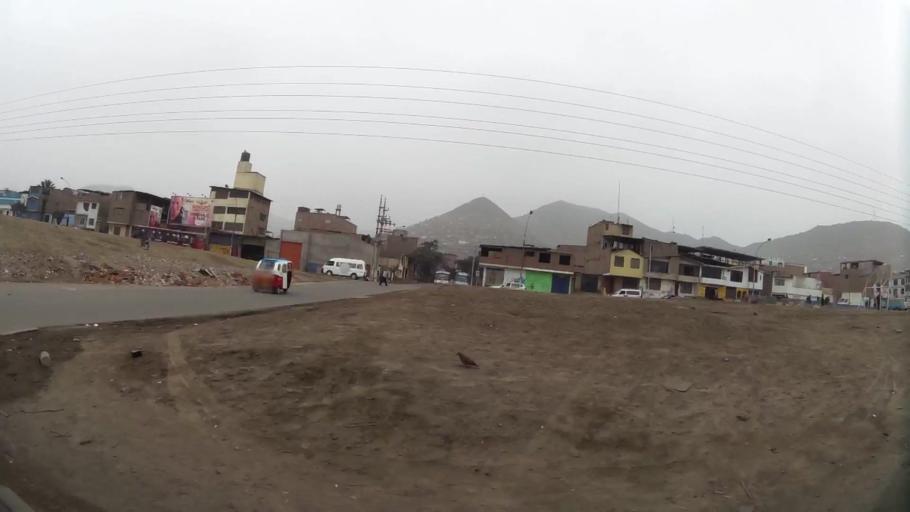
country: PE
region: Lima
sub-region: Lima
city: Surco
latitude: -12.1704
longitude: -76.9470
